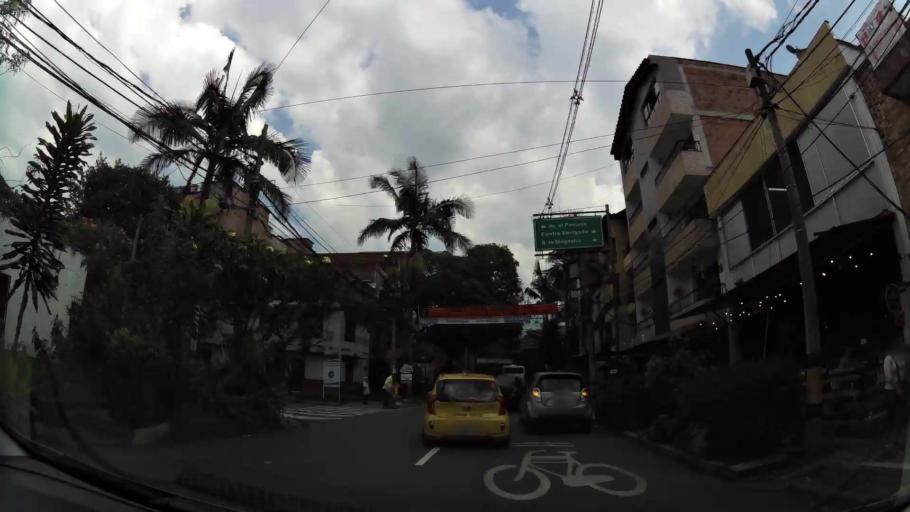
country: CO
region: Antioquia
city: Envigado
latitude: 6.1777
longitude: -75.5862
